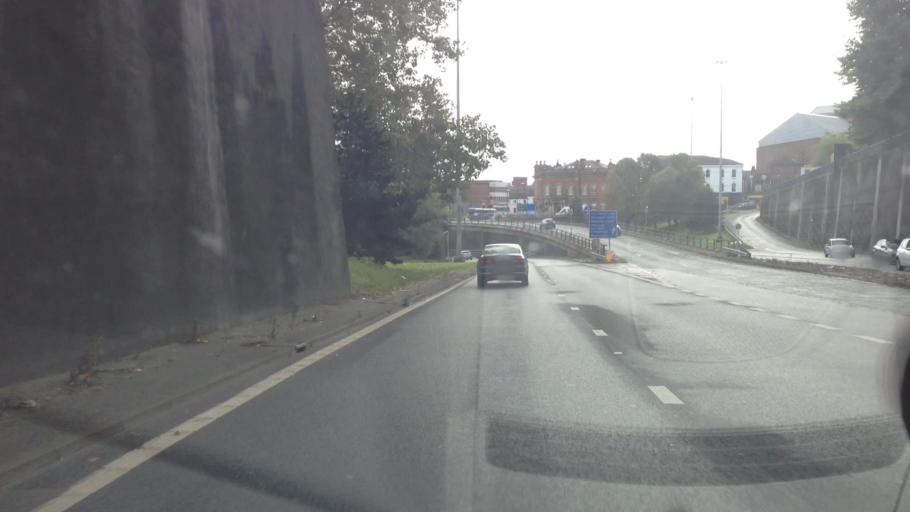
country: GB
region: England
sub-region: City and Borough of Leeds
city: Leeds
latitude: 53.8029
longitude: -1.5403
